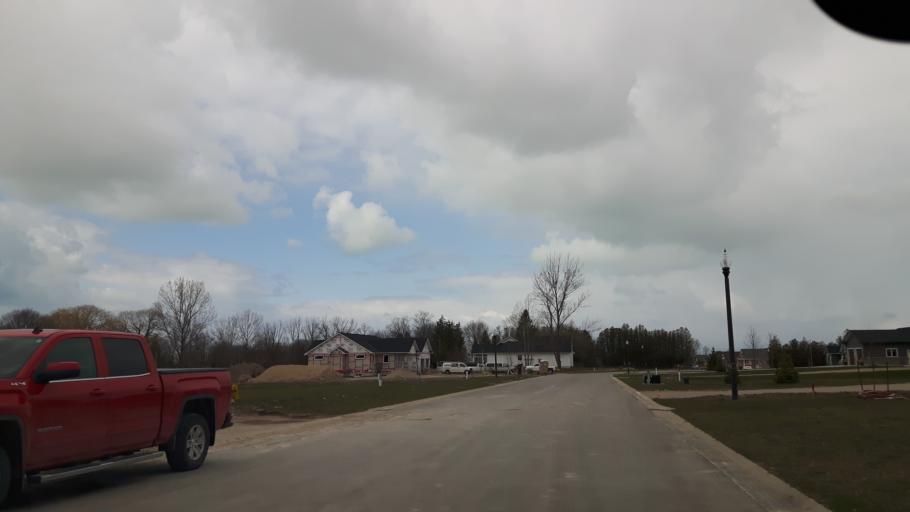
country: CA
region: Ontario
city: Bluewater
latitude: 43.5512
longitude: -81.6977
